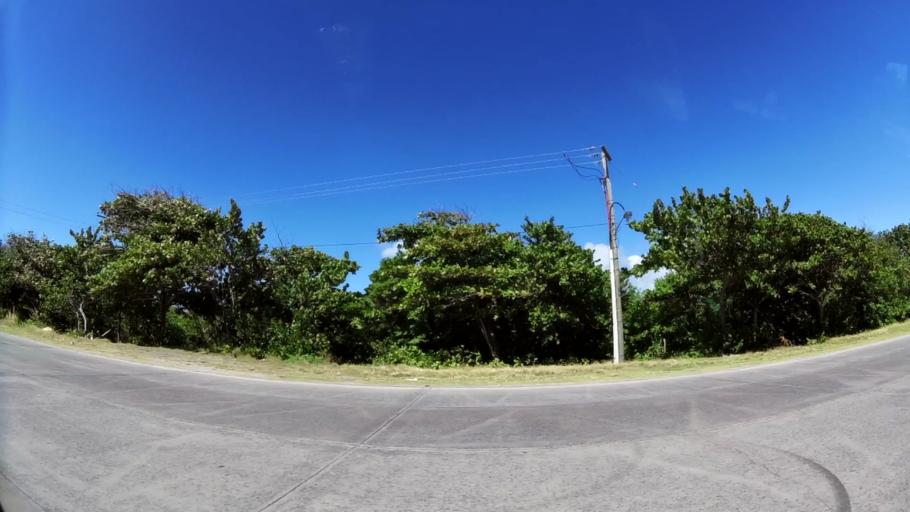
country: LC
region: Vieux-Fort
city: Vieux Fort
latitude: 13.7316
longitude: -60.9419
